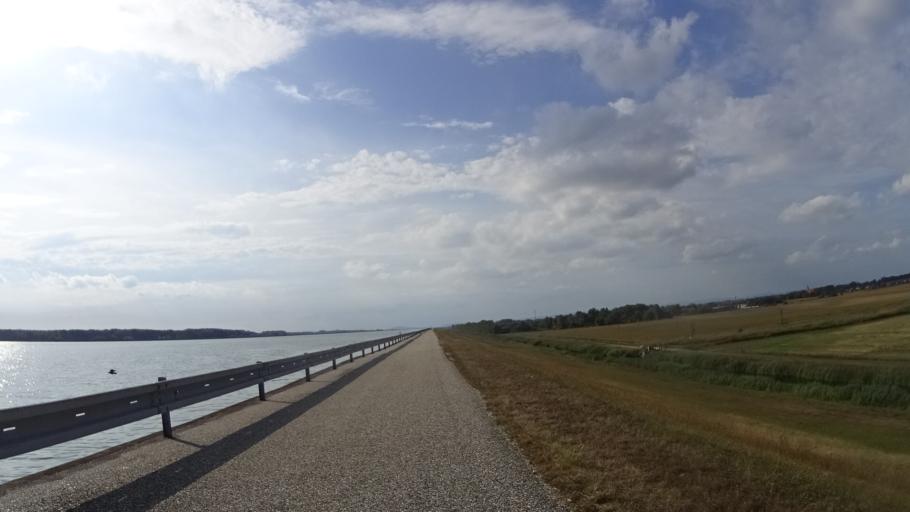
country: HU
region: Gyor-Moson-Sopron
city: Asvanyraro
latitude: 47.9331
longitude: 17.4663
